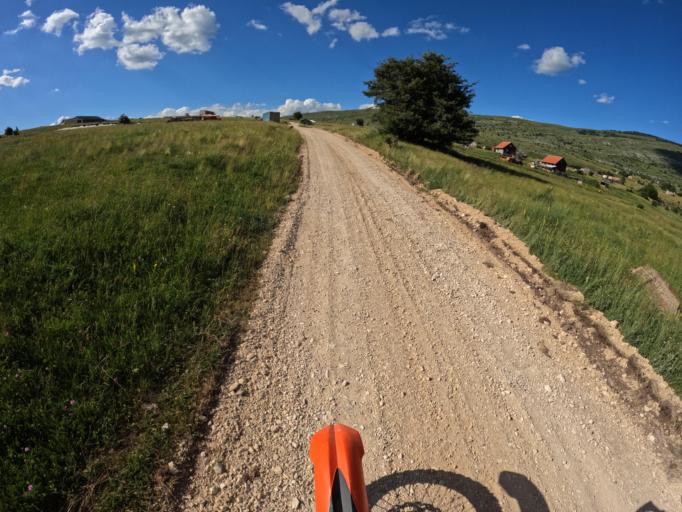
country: BA
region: Federation of Bosnia and Herzegovina
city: Glamoc
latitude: 44.1390
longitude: 16.9590
